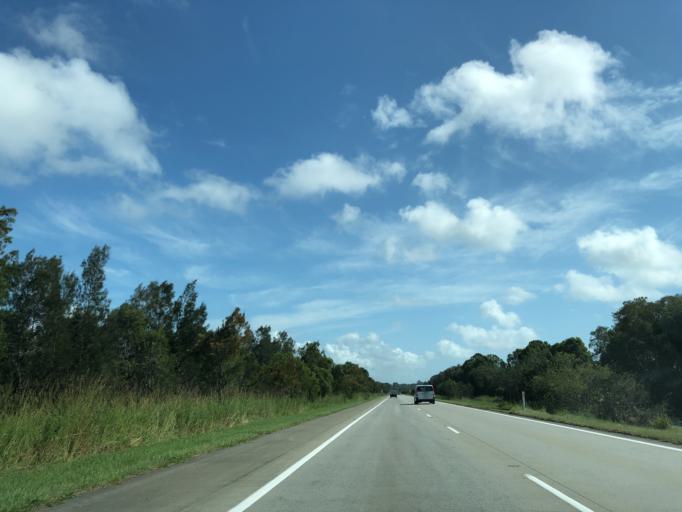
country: AU
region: New South Wales
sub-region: Byron Shire
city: Brunswick Heads
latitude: -28.5934
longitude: 153.5446
